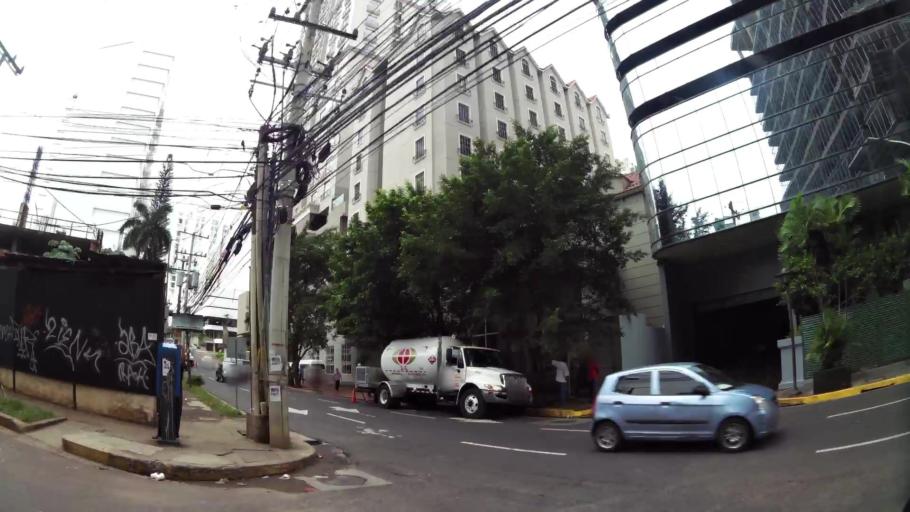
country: PA
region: Panama
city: Panama
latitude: 8.9803
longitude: -79.5250
